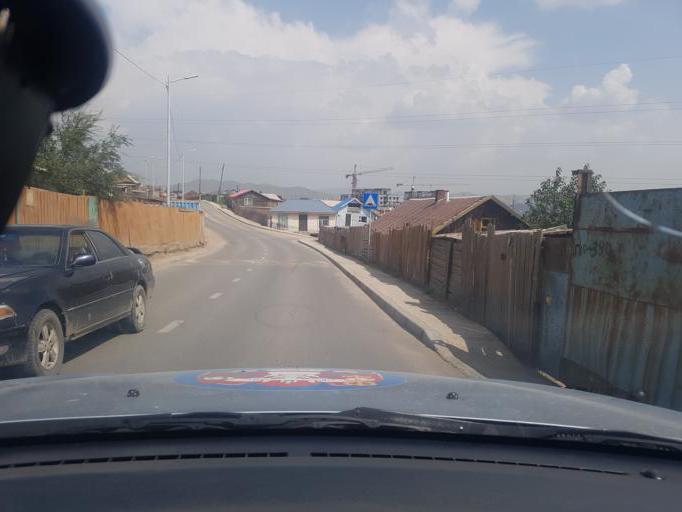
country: MN
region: Ulaanbaatar
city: Ulaanbaatar
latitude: 47.9360
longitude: 106.8965
